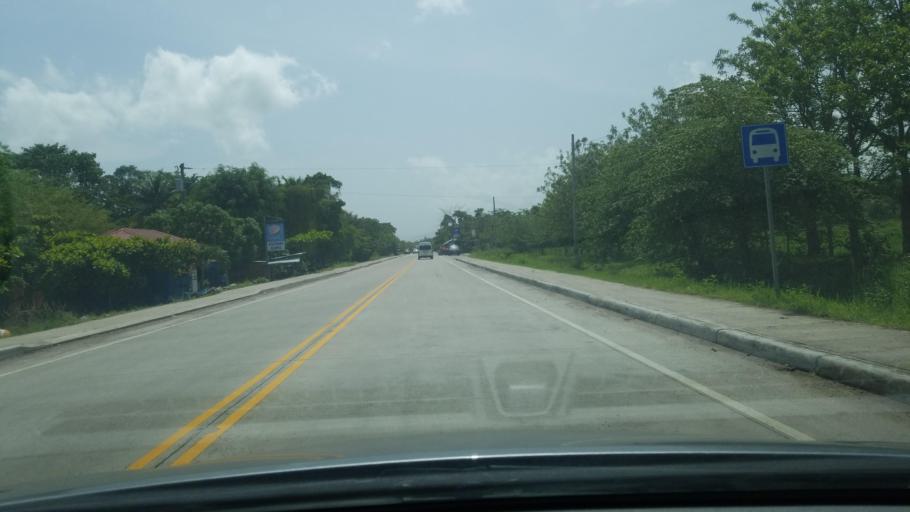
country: HN
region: Copan
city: Florida
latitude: 15.0445
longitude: -88.8110
